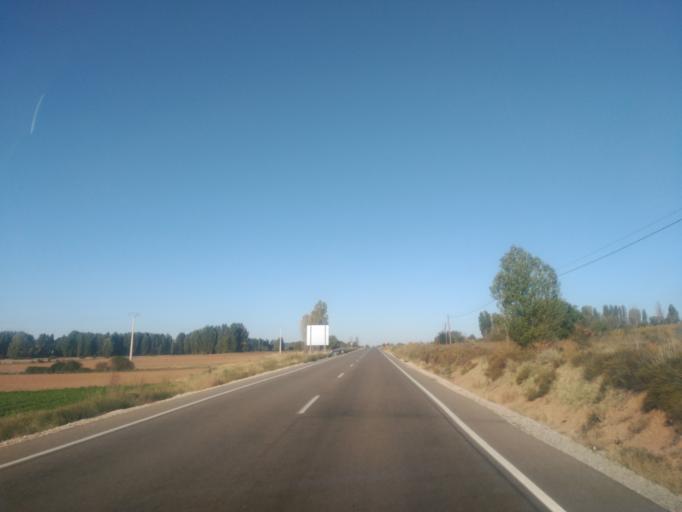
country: ES
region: Castille and Leon
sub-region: Provincia de Burgos
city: Penaranda de Duero
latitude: 41.6861
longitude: -3.4984
